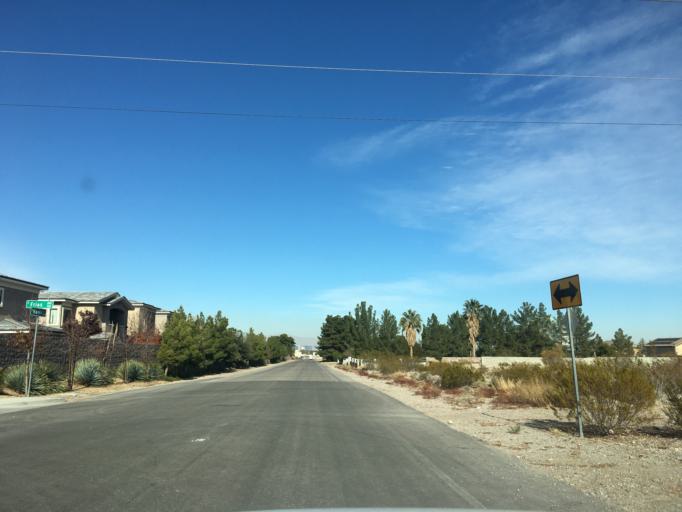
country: US
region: Nevada
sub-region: Clark County
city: Enterprise
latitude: 36.0028
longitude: -115.1681
